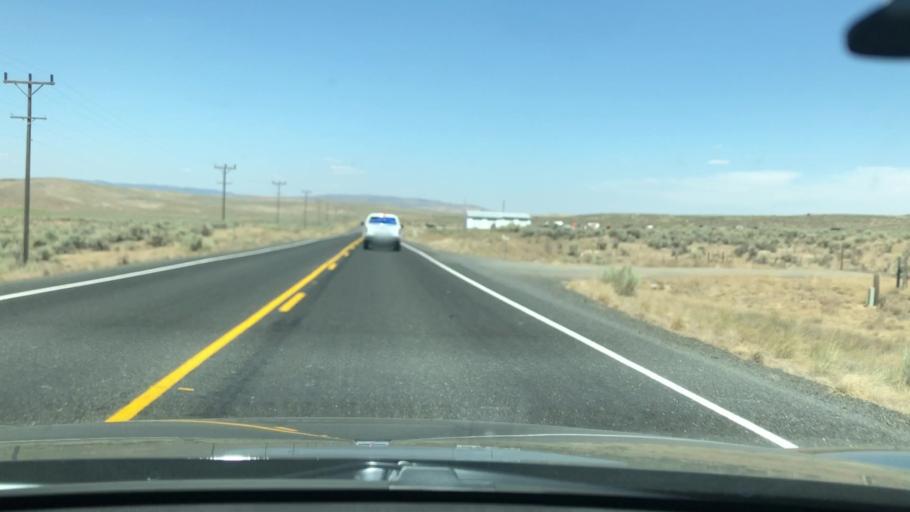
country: US
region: Idaho
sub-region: Owyhee County
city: Murphy
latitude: 42.9991
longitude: -117.0644
